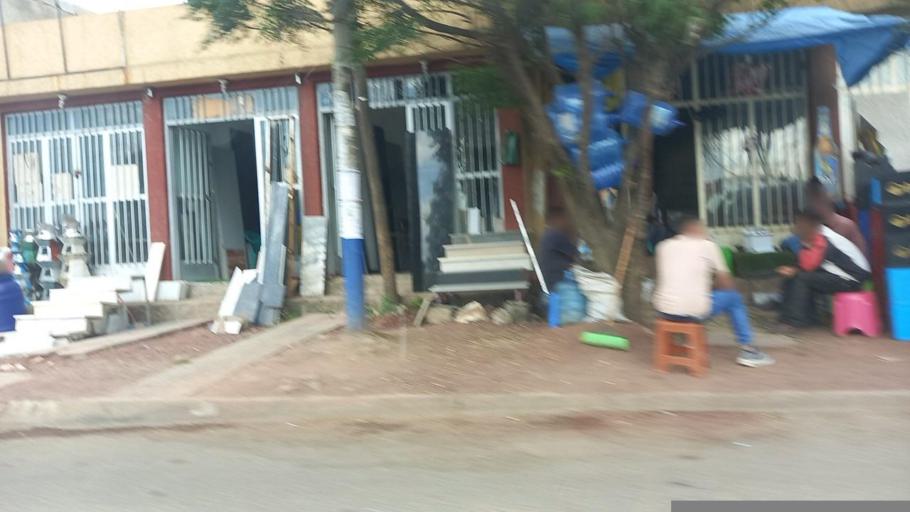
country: ET
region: Adis Abeba
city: Addis Ababa
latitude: 9.0145
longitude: 38.8314
